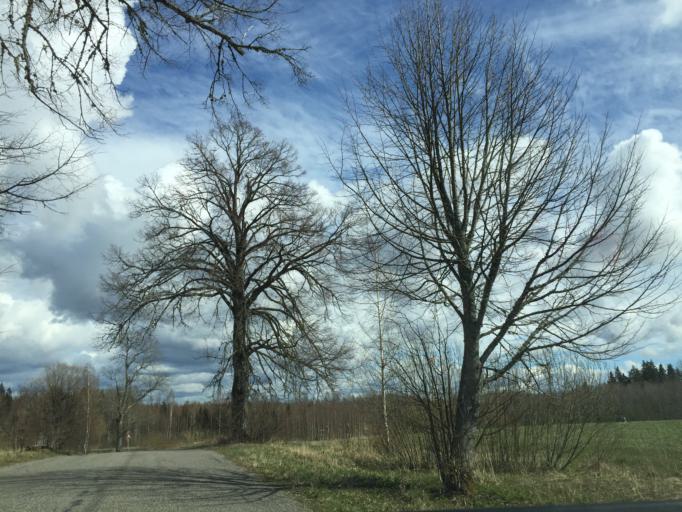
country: LV
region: Limbazu Rajons
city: Limbazi
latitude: 57.6132
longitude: 24.6801
